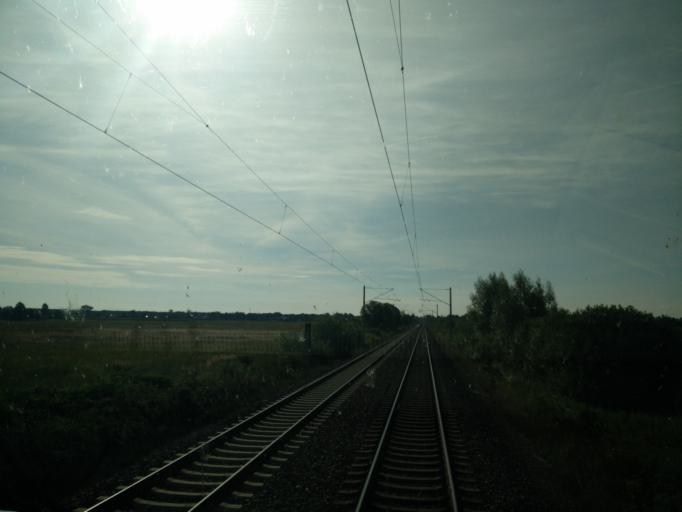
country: DE
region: Brandenburg
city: Luebben
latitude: 51.9685
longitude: 13.8120
